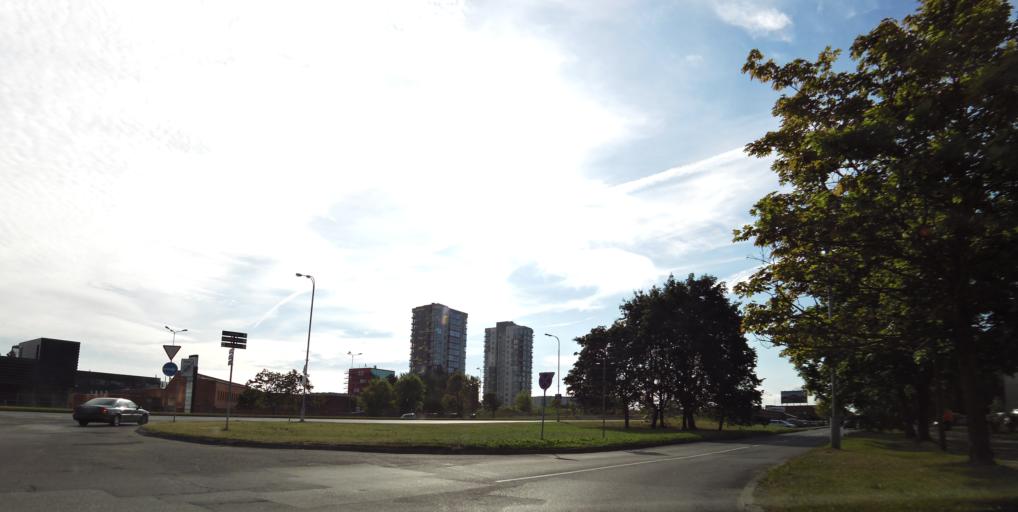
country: LT
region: Vilnius County
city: Seskine
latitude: 54.7149
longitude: 25.2469
